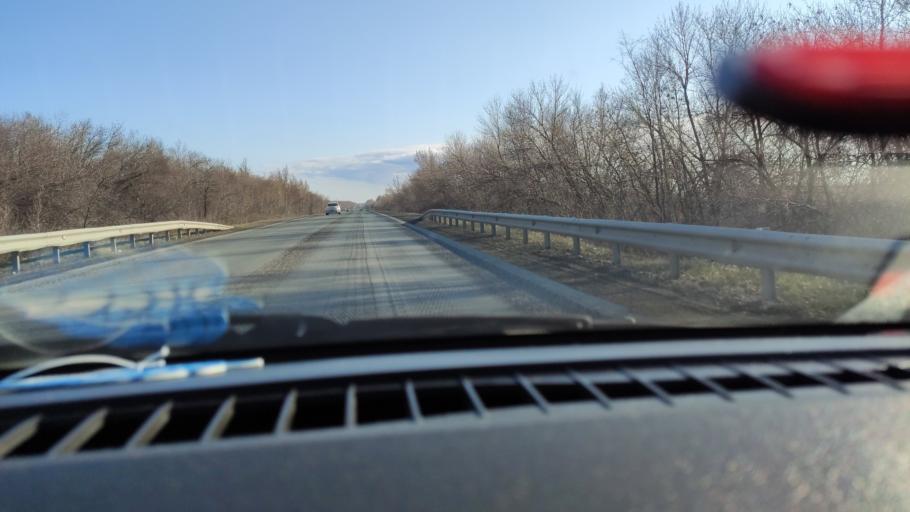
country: RU
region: Saratov
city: Dukhovnitskoye
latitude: 52.6564
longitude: 48.2060
